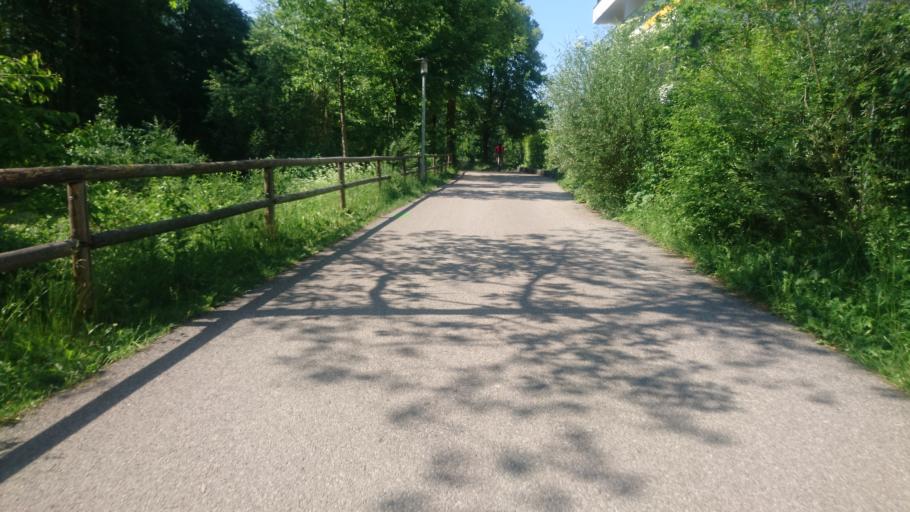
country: DE
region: Bavaria
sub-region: Upper Bavaria
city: Pullach im Isartal
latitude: 48.0988
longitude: 11.5465
